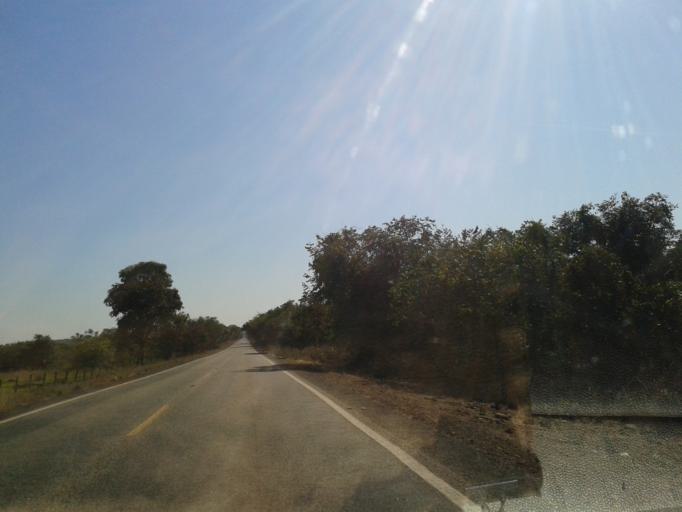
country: BR
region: Goias
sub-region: Mozarlandia
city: Mozarlandia
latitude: -14.5868
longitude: -50.5066
